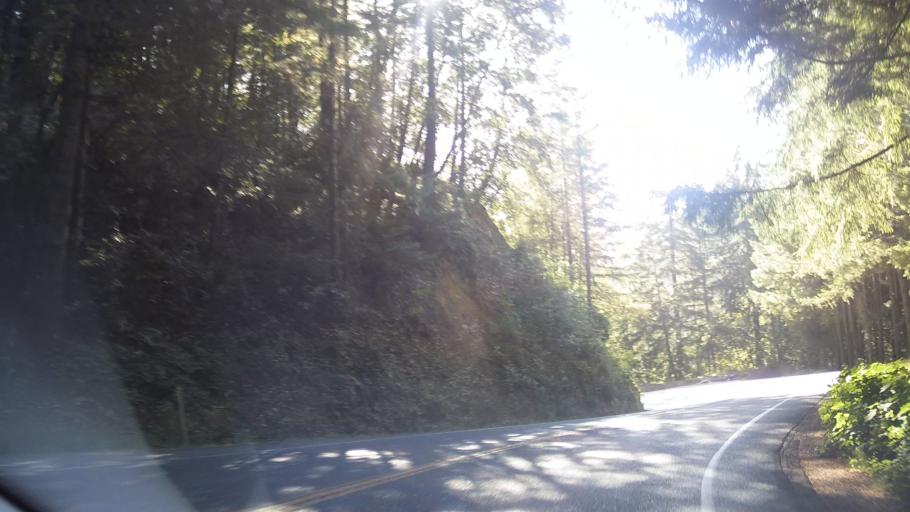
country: US
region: California
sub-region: Mendocino County
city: Brooktrails
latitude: 39.3630
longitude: -123.5024
